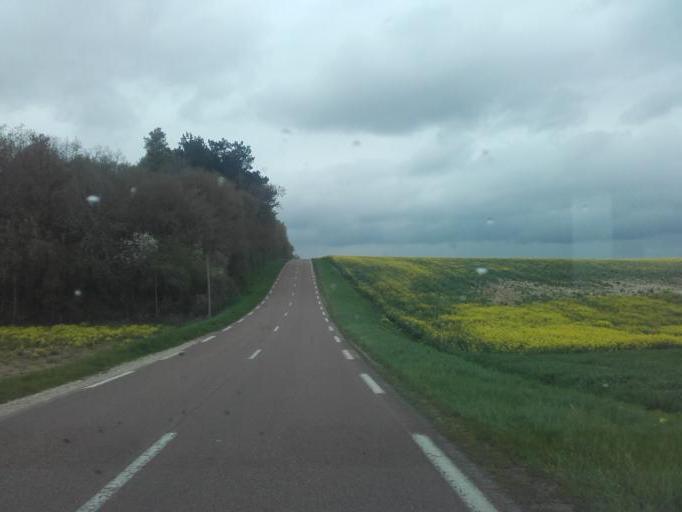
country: FR
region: Bourgogne
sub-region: Departement de l'Yonne
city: Joux-la-Ville
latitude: 47.6902
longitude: 3.8659
